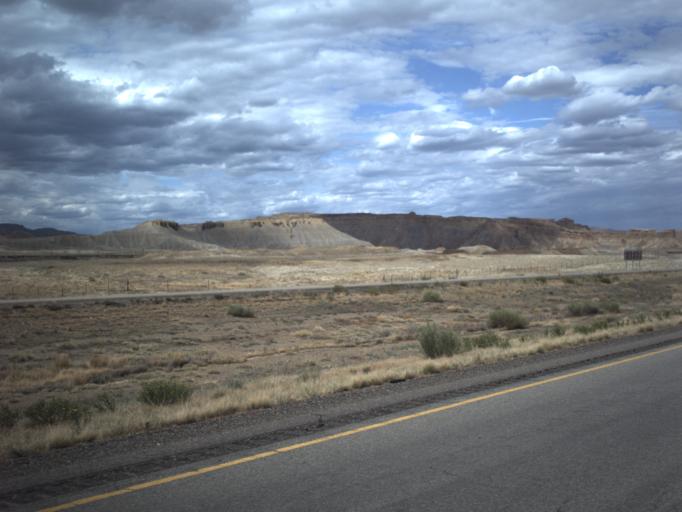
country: US
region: Utah
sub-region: Grand County
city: Moab
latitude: 38.9241
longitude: -109.9148
